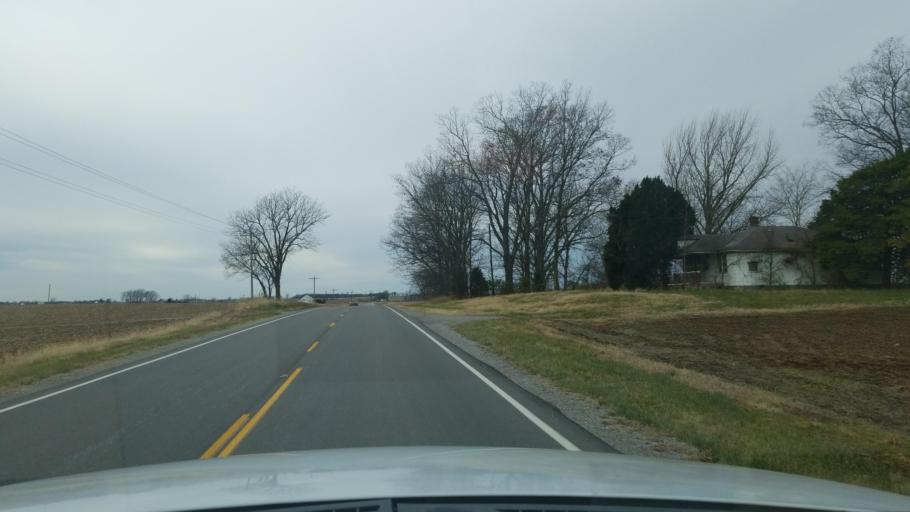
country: US
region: Illinois
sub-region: White County
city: Norris City
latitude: 37.9076
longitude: -88.1640
